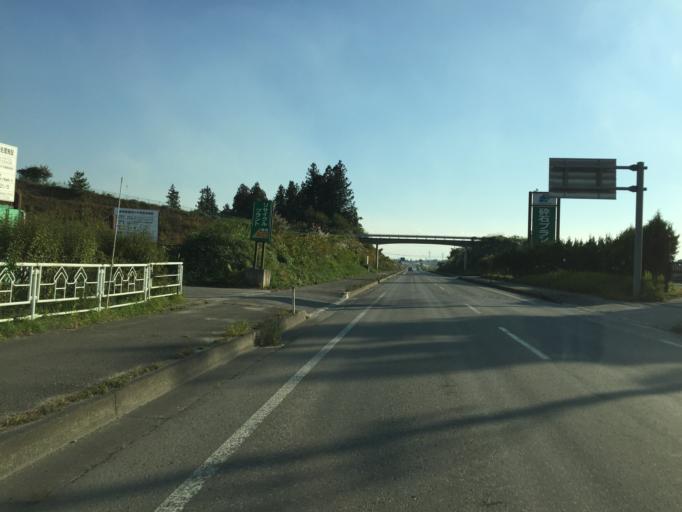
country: JP
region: Fukushima
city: Kitakata
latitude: 37.6871
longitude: 139.8898
